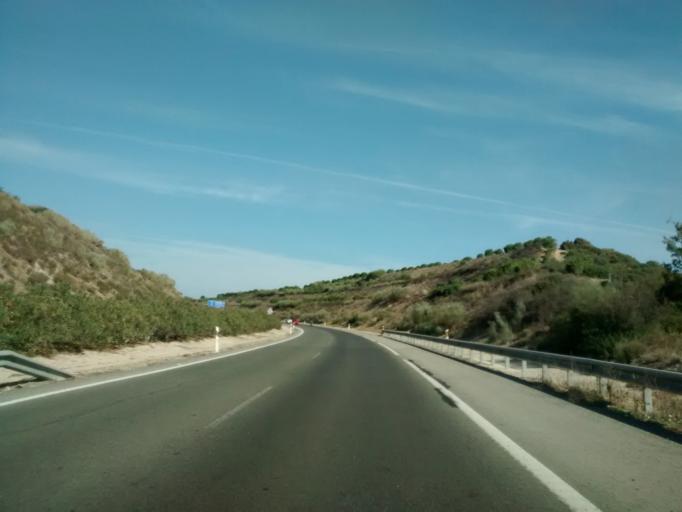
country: ES
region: Andalusia
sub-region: Provincia de Cadiz
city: Conil de la Frontera
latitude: 36.3402
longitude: -6.0494
